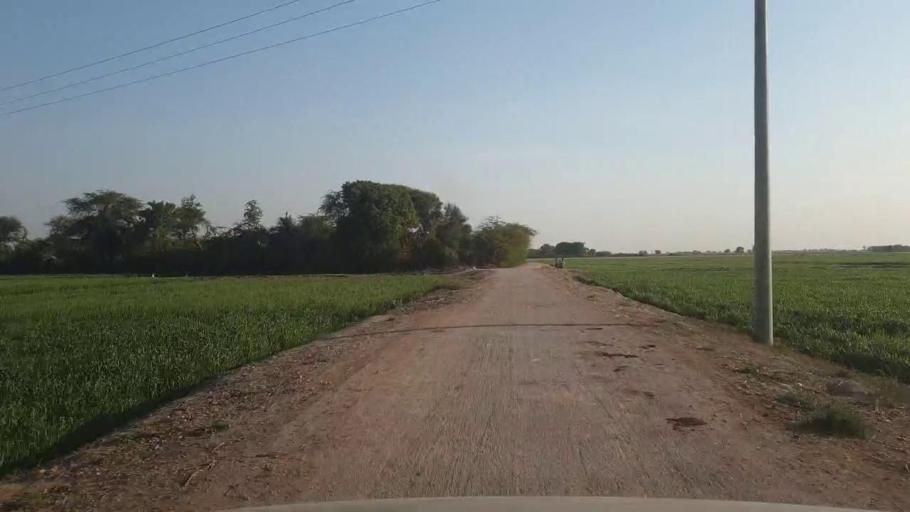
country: PK
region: Sindh
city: Chambar
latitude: 25.2525
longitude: 68.8847
